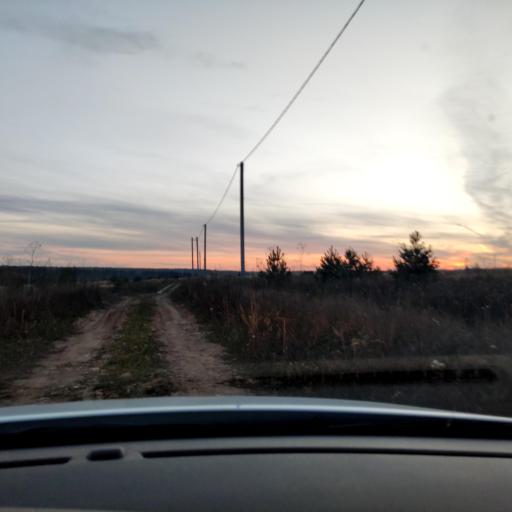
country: RU
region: Tatarstan
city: Vysokaya Gora
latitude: 55.9666
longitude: 49.2069
